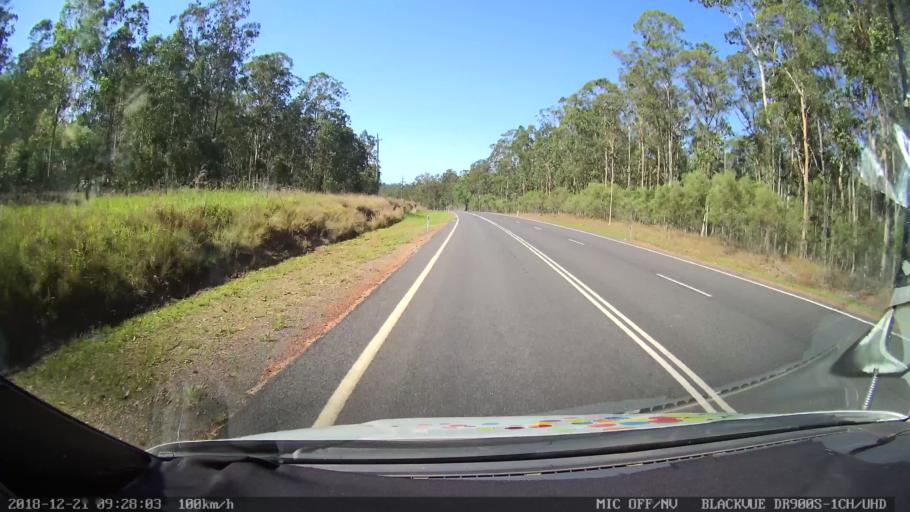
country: AU
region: New South Wales
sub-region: Clarence Valley
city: Maclean
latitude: -29.4116
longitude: 152.9871
